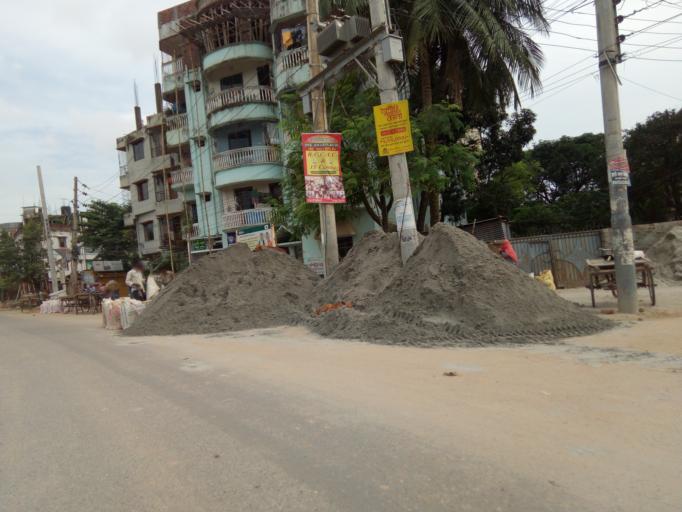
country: BD
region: Dhaka
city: Tungi
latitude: 23.8469
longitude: 90.4193
